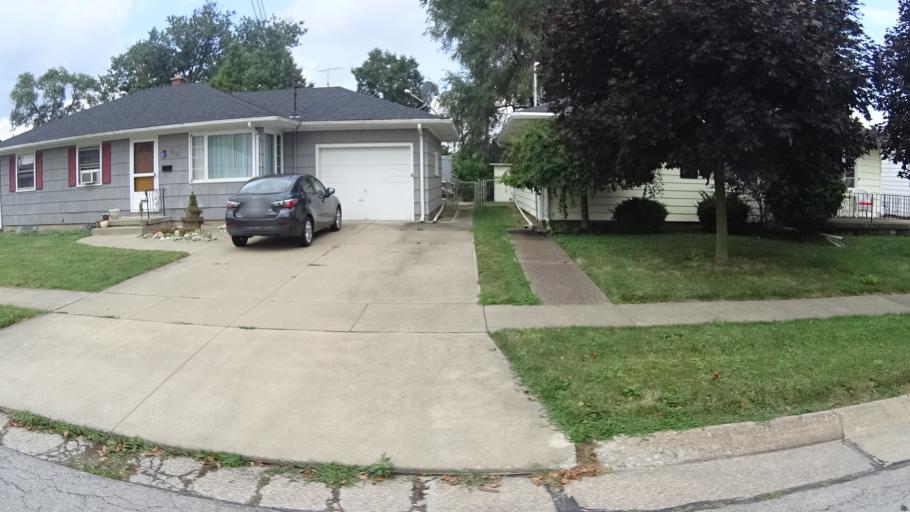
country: US
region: Ohio
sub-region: Erie County
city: Sandusky
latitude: 41.4348
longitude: -82.7253
